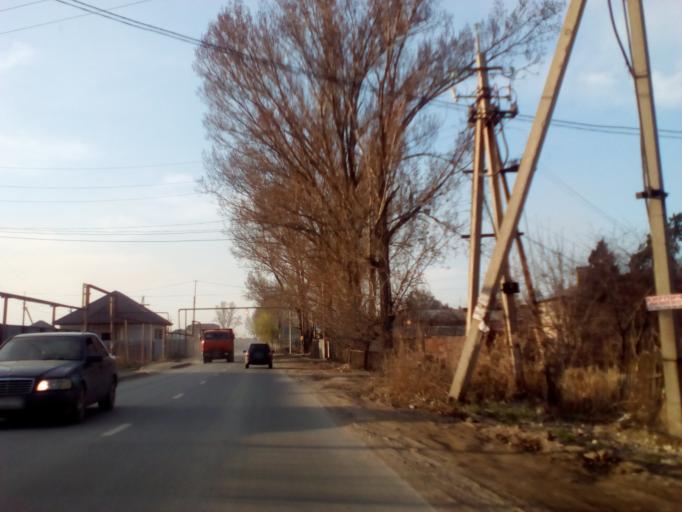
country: KZ
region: Almaty Oblysy
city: Burunday
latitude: 43.2415
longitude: 76.7887
